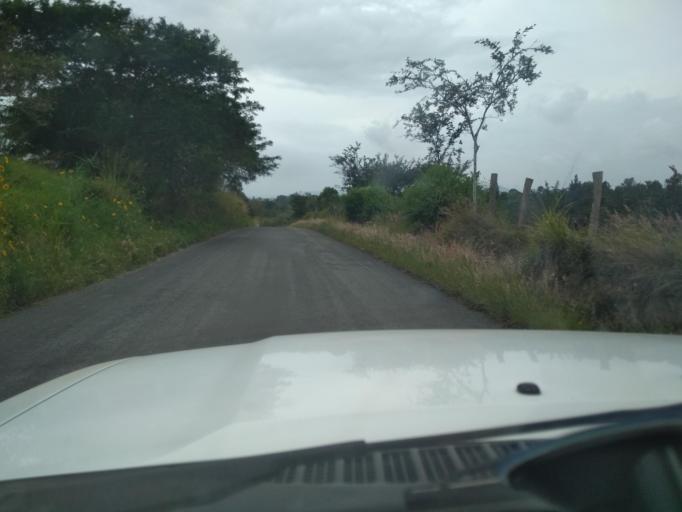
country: MX
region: Veracruz
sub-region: Emiliano Zapata
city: Dos Rios
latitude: 19.5308
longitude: -96.7986
